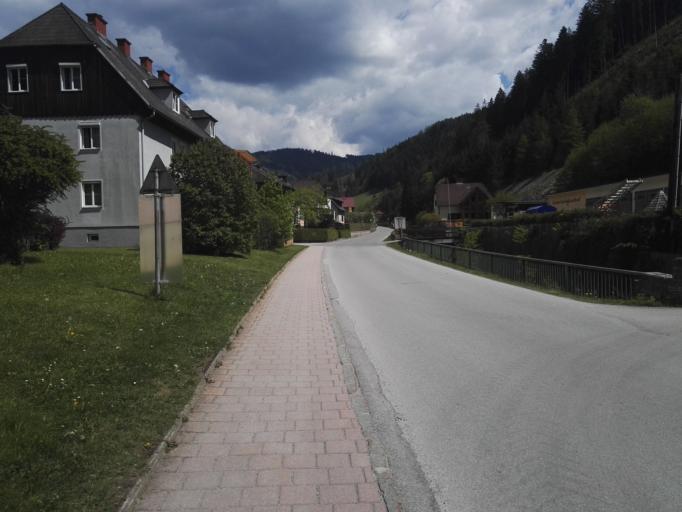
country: AT
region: Styria
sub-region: Politischer Bezirk Bruck-Muerzzuschlag
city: Allerheiligen im Muerztal
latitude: 47.3940
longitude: 15.4310
